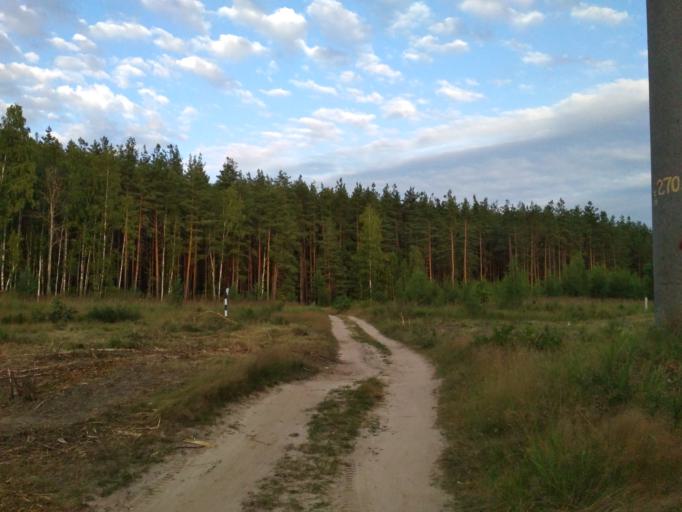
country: RU
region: Rjazan
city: Solotcha
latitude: 54.8303
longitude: 39.9448
